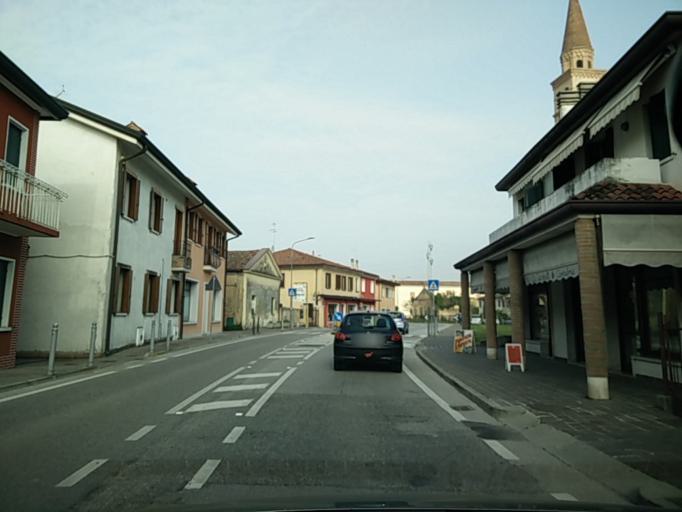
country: IT
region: Veneto
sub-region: Provincia di Venezia
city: Scaltenigo
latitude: 45.4704
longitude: 12.0812
